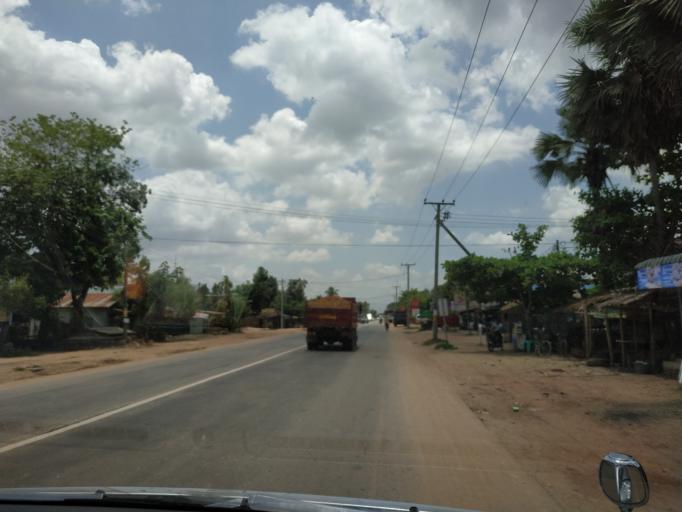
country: MM
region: Bago
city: Bago
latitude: 17.4739
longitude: 96.5315
